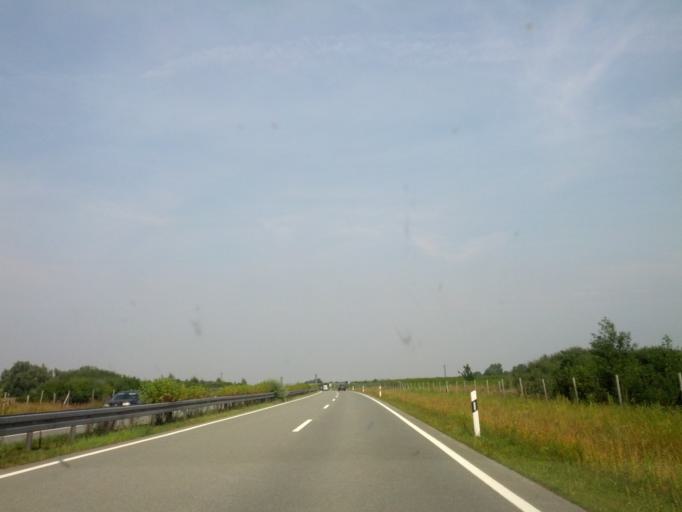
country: DE
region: Mecklenburg-Vorpommern
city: Grimmen
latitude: 54.0947
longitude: 13.1360
